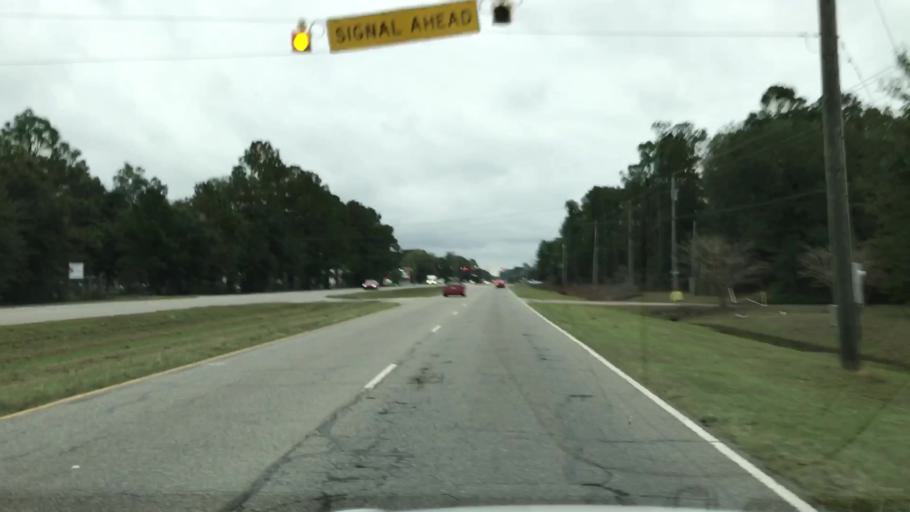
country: US
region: South Carolina
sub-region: Georgetown County
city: Georgetown
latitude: 33.3245
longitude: -79.3183
